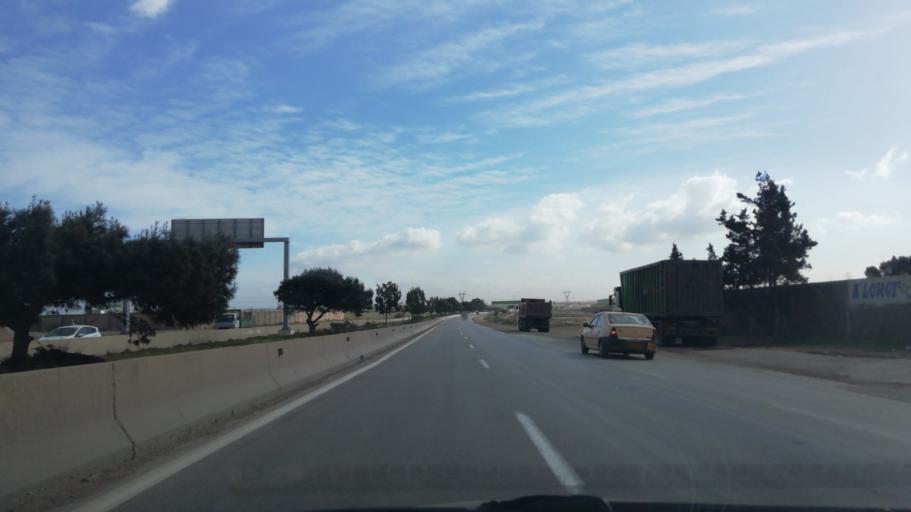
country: DZ
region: Oran
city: Ain el Bya
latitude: 35.7798
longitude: -0.2721
